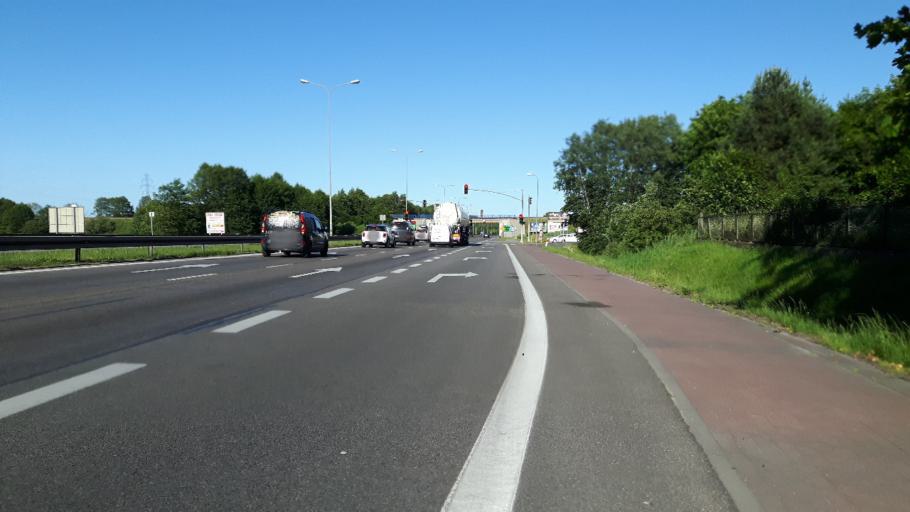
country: PL
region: Pomeranian Voivodeship
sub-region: Powiat wejherowski
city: Reda
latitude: 54.6049
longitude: 18.3370
